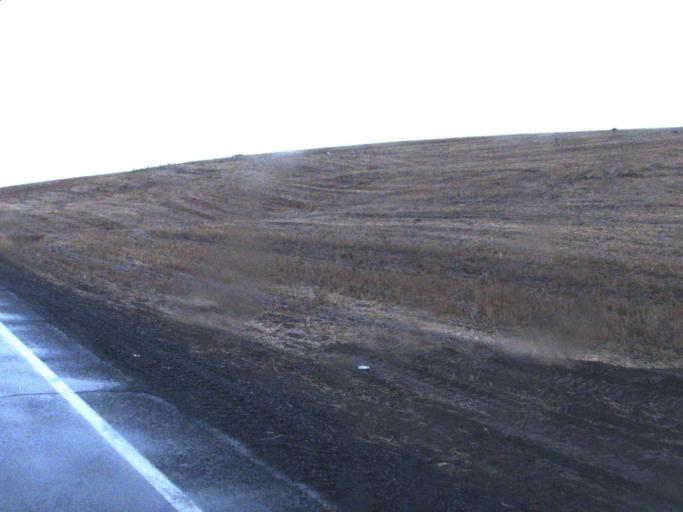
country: US
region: Washington
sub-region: Lincoln County
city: Davenport
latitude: 47.4663
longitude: -118.1842
